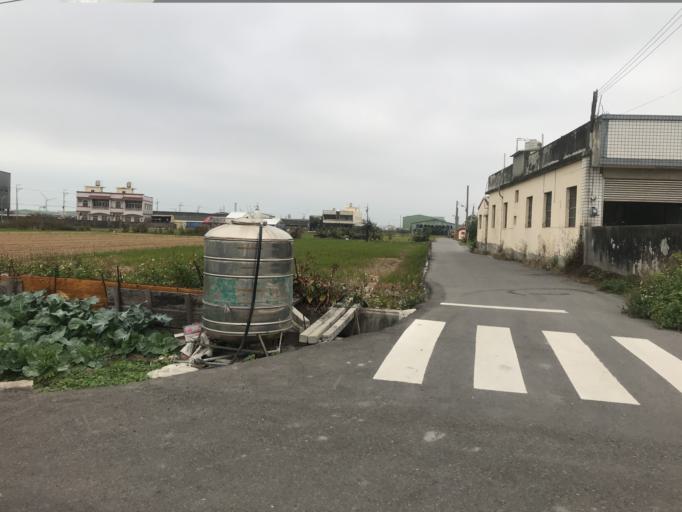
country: TW
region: Taiwan
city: Fengyuan
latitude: 24.3750
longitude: 120.5974
